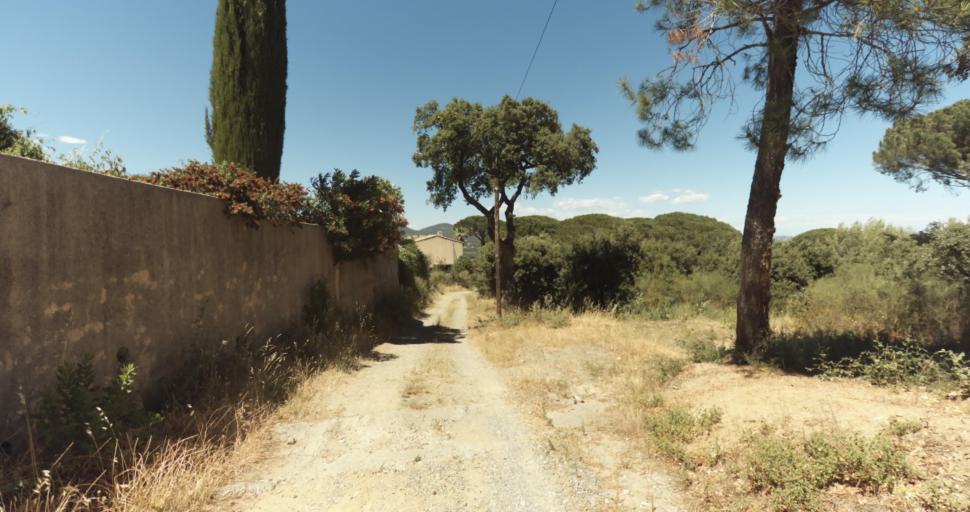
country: FR
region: Provence-Alpes-Cote d'Azur
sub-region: Departement du Var
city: Gassin
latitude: 43.2557
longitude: 6.5656
